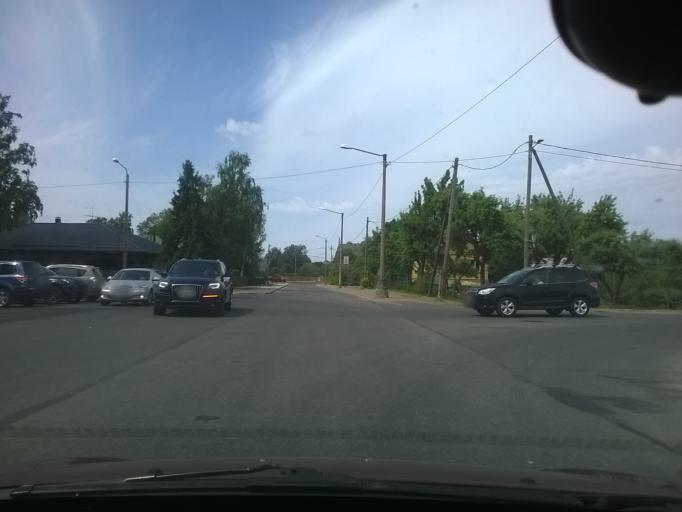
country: EE
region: Harju
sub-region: Tallinna linn
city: Tallinn
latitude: 59.4250
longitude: 24.6894
